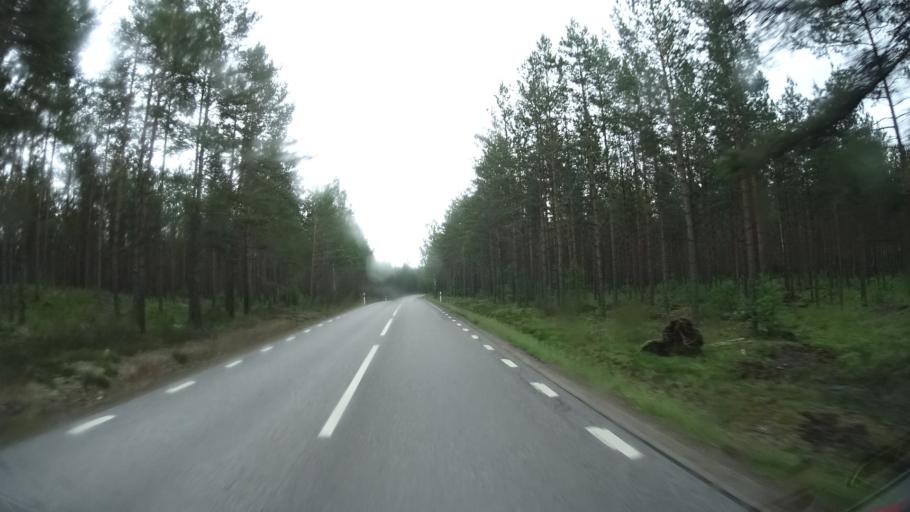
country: SE
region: Kalmar
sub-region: Hultsfreds Kommun
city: Hultsfred
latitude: 57.5293
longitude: 15.7828
